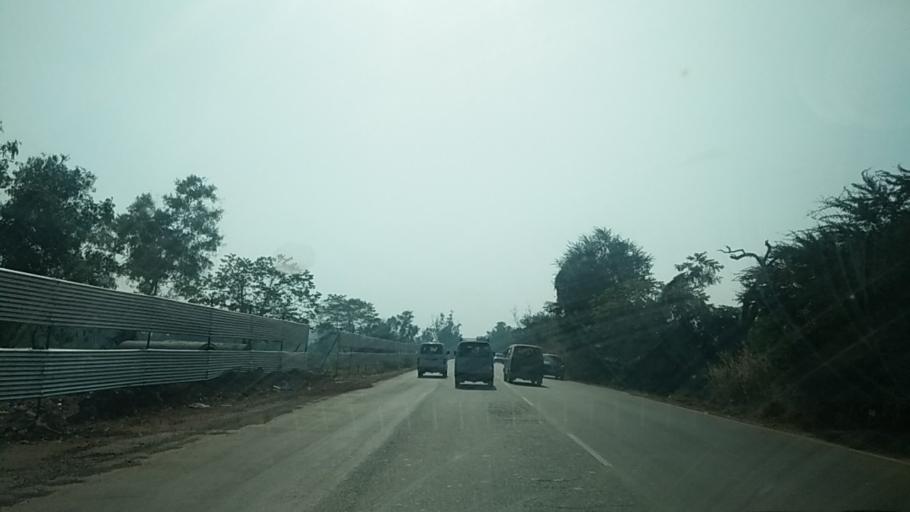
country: IN
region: Goa
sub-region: North Goa
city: Guirim
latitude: 15.5800
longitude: 73.8127
